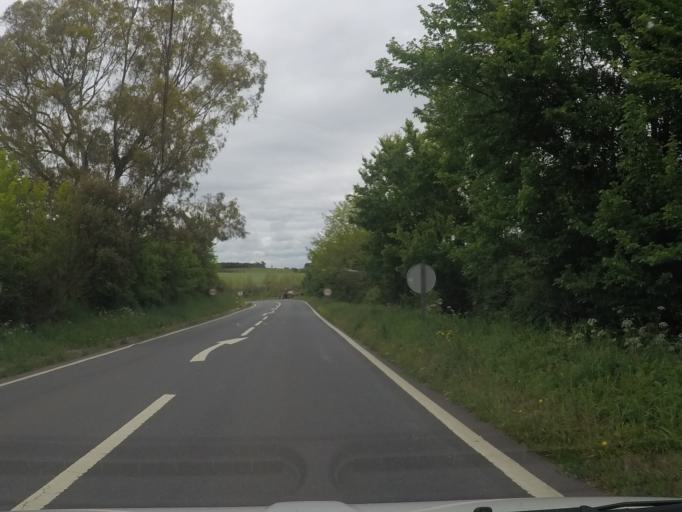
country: PT
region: Setubal
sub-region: Santiago do Cacem
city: Cercal
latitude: 37.8175
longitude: -8.6834
